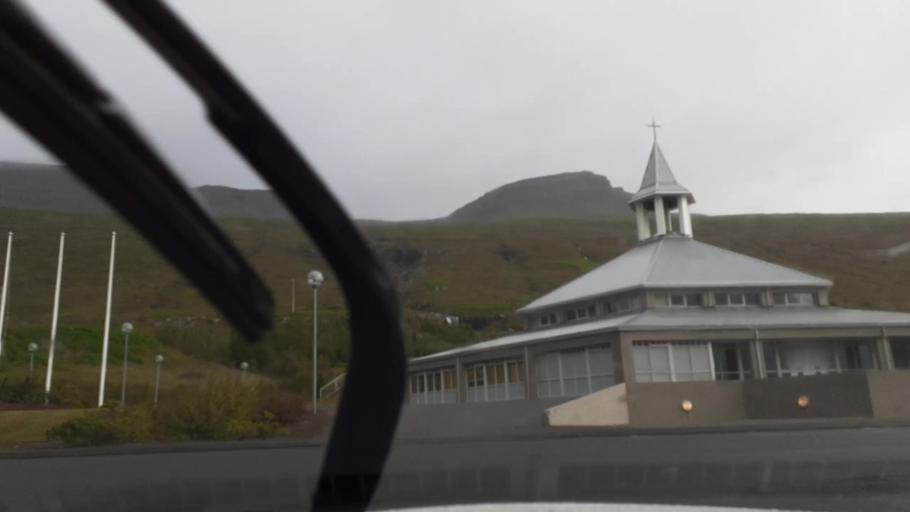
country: IS
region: East
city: Eskifjoerdur
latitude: 65.0784
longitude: -14.0342
